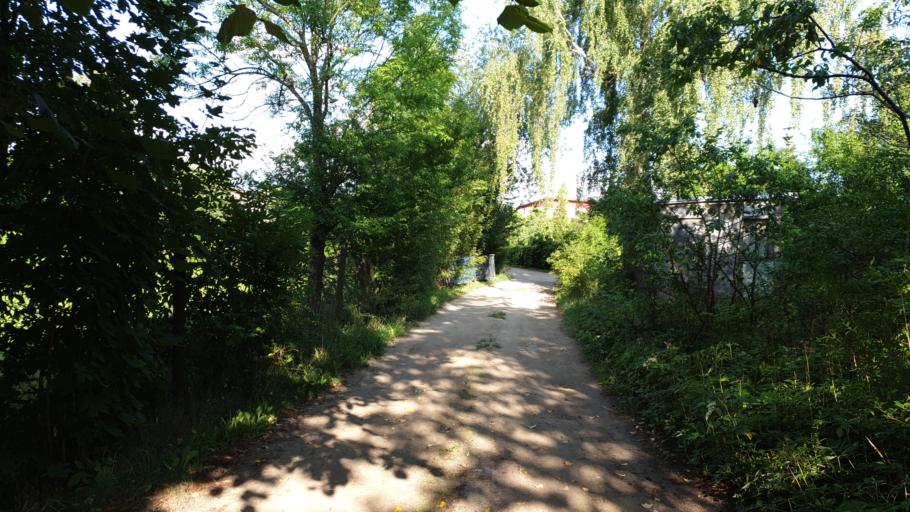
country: LT
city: Grigiskes
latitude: 54.7684
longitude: 25.0210
